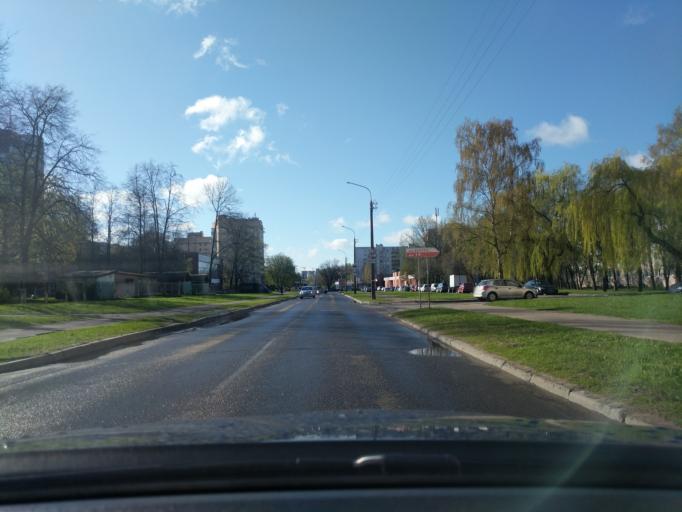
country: BY
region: Minsk
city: Novoye Medvezhino
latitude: 53.9030
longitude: 27.5039
